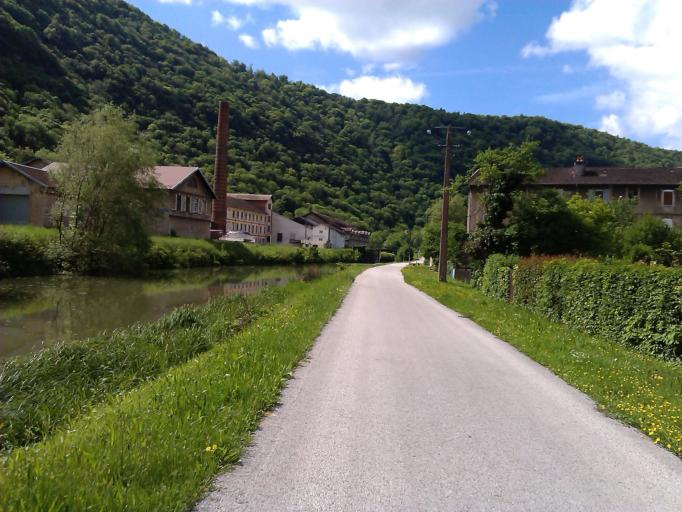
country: FR
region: Franche-Comte
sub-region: Departement du Doubs
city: Roulans
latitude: 47.2943
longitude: 6.2038
